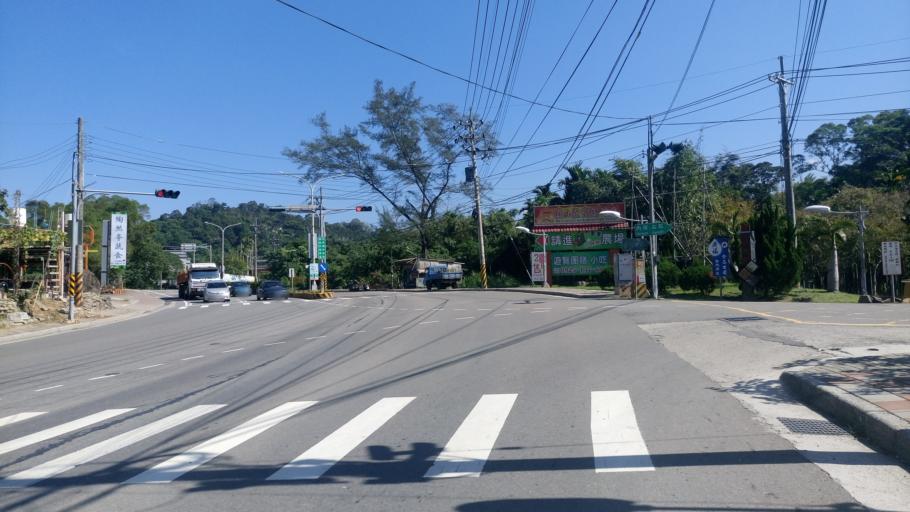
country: TW
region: Taiwan
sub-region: Hsinchu
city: Zhubei
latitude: 24.7167
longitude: 121.1439
